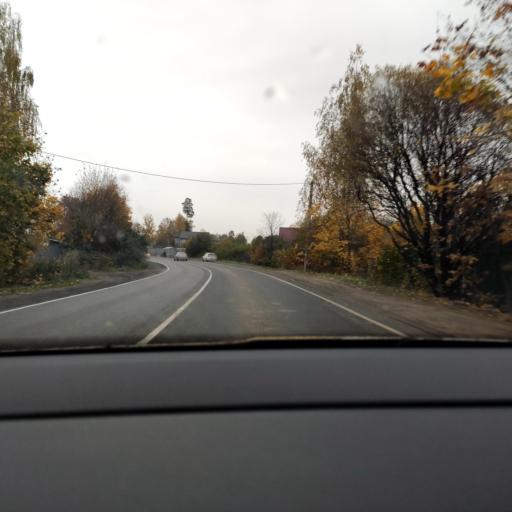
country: RU
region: Moskovskaya
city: Lesnyye Polyany
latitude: 55.9697
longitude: 37.8716
